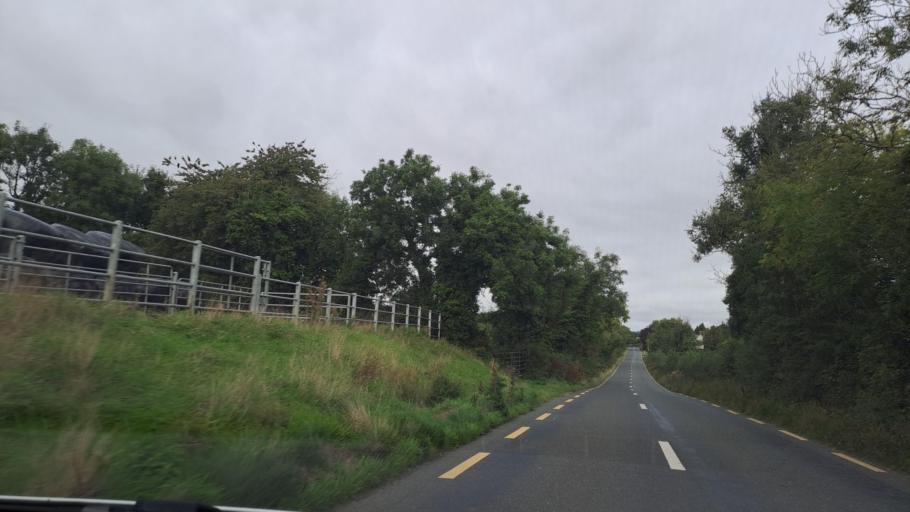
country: IE
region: Ulster
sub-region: An Cabhan
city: Kingscourt
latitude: 53.8905
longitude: -6.7544
